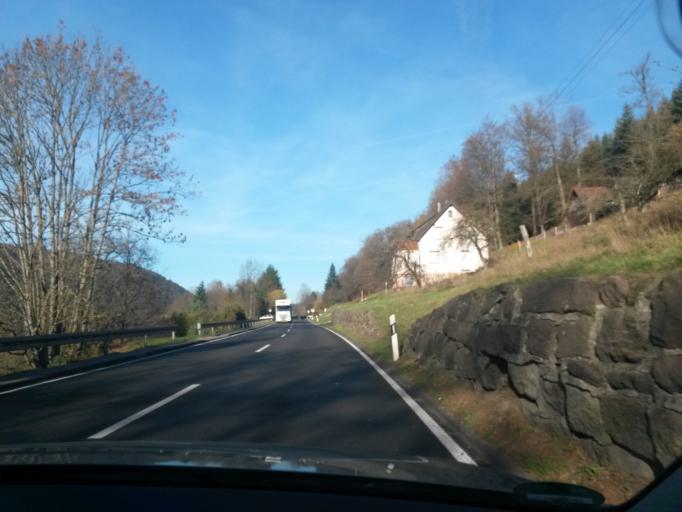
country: DE
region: Baden-Wuerttemberg
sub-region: Karlsruhe Region
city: Hofen an der Enz
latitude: 48.7823
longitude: 8.5791
